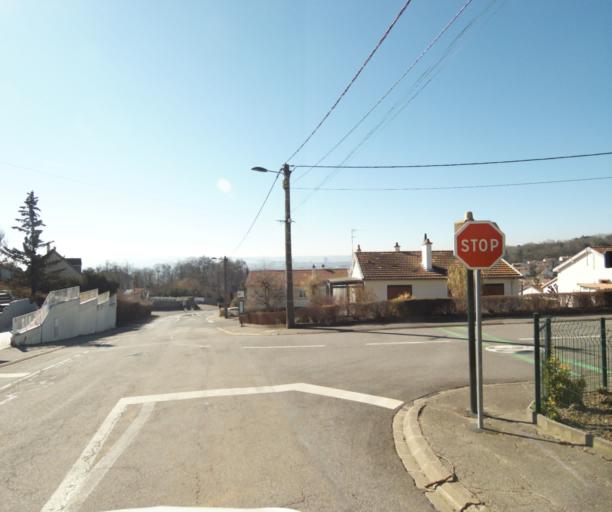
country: FR
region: Lorraine
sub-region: Departement de Meurthe-et-Moselle
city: Essey-les-Nancy
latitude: 48.7107
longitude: 6.2222
